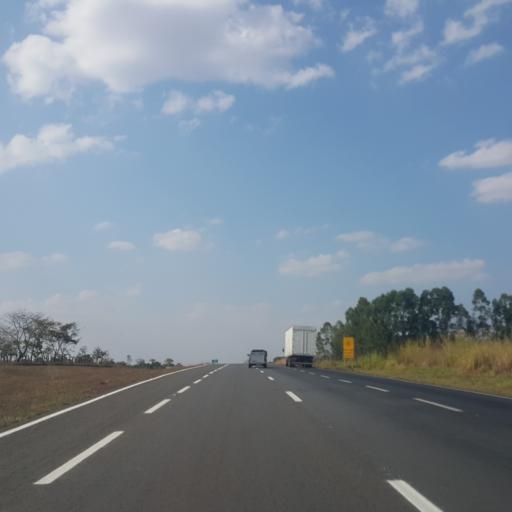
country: BR
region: Goias
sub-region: Abadiania
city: Abadiania
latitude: -16.2855
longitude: -48.7963
